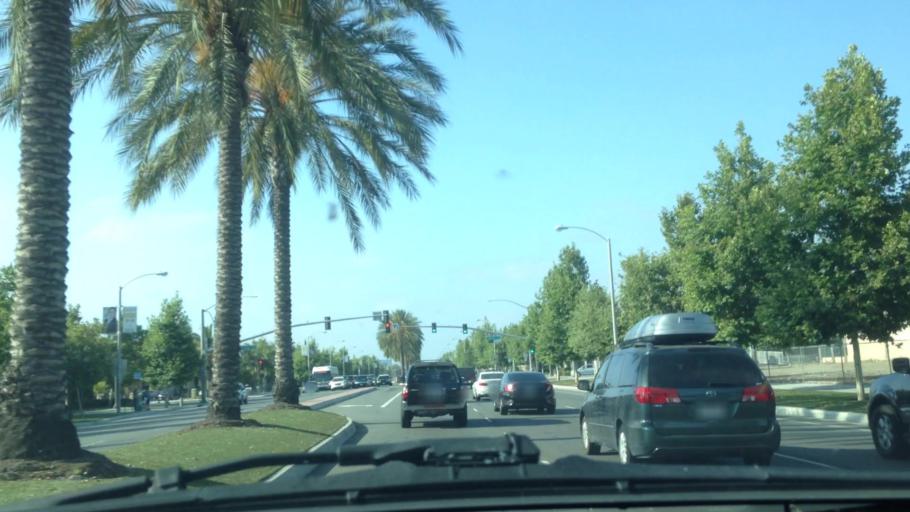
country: US
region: California
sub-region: Orange County
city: Santa Ana
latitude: 33.7409
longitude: -117.8853
